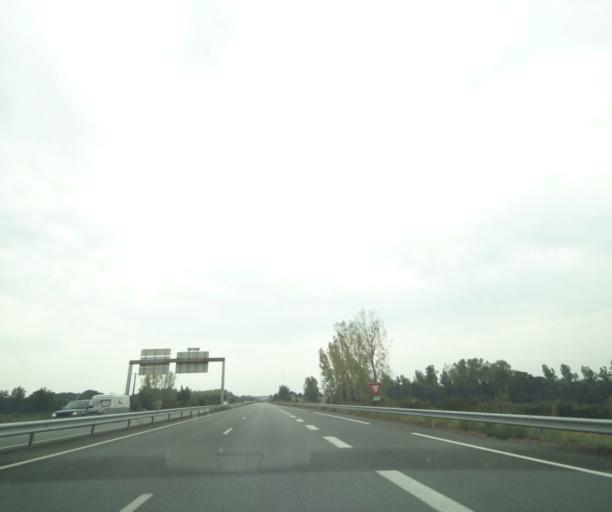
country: FR
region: Pays de la Loire
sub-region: Departement de la Vendee
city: Bournezeau
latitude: 46.6245
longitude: -1.1465
